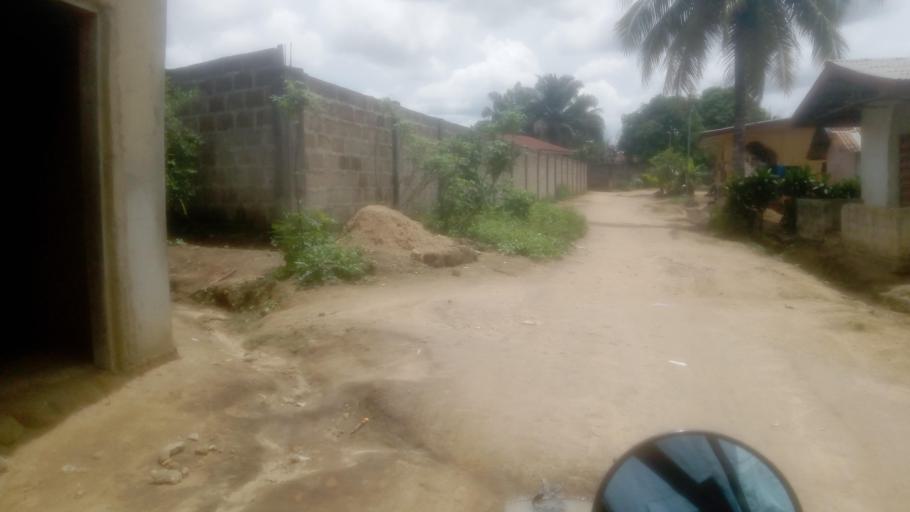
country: SL
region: Southern Province
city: Bo
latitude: 7.9526
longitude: -11.7131
